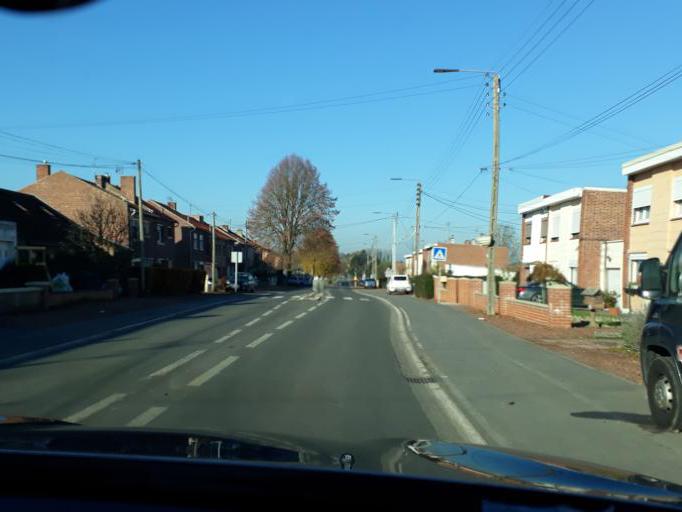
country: FR
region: Nord-Pas-de-Calais
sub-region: Departement du Nord
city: Masny
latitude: 50.3519
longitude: 3.2010
